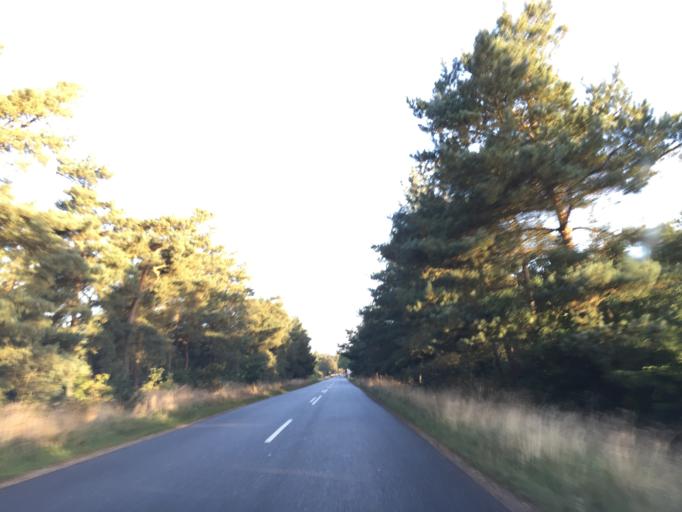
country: DK
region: Central Jutland
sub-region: Viborg Kommune
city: Bjerringbro
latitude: 56.2930
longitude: 9.6733
